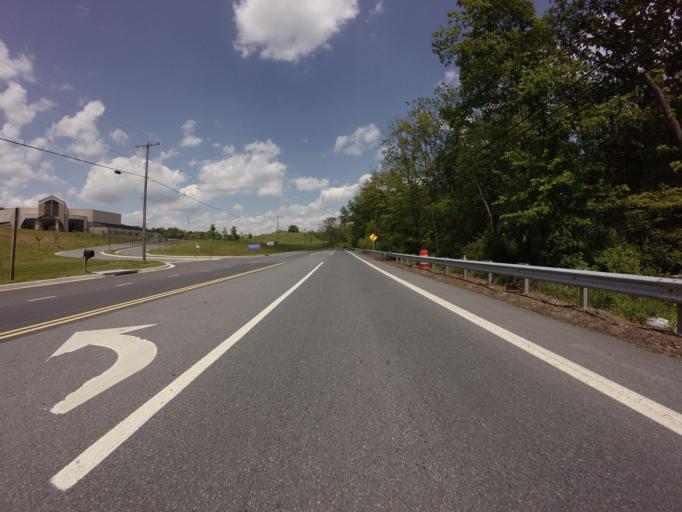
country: US
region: Maryland
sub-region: Frederick County
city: Green Valley
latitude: 39.3176
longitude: -77.2903
